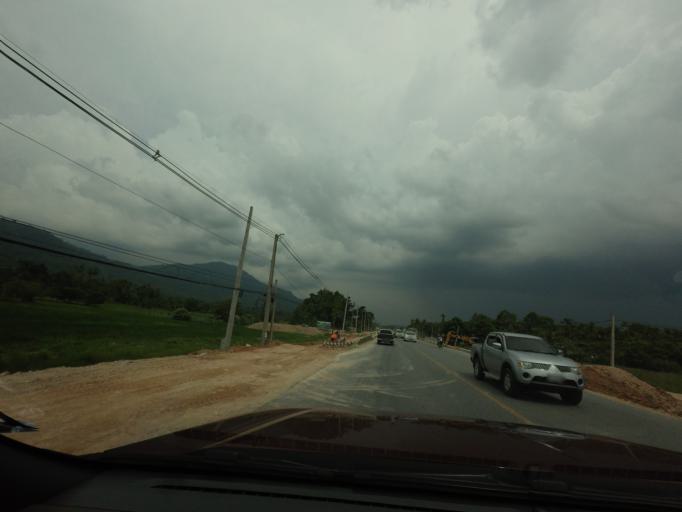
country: TH
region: Yala
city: Krong Pi Nang
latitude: 6.4502
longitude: 101.2757
